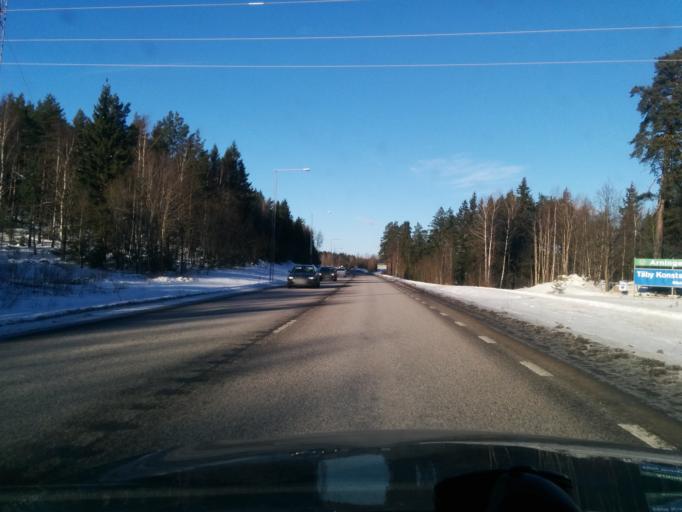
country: SE
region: Stockholm
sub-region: Taby Kommun
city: Taby
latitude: 59.4778
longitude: 18.1206
